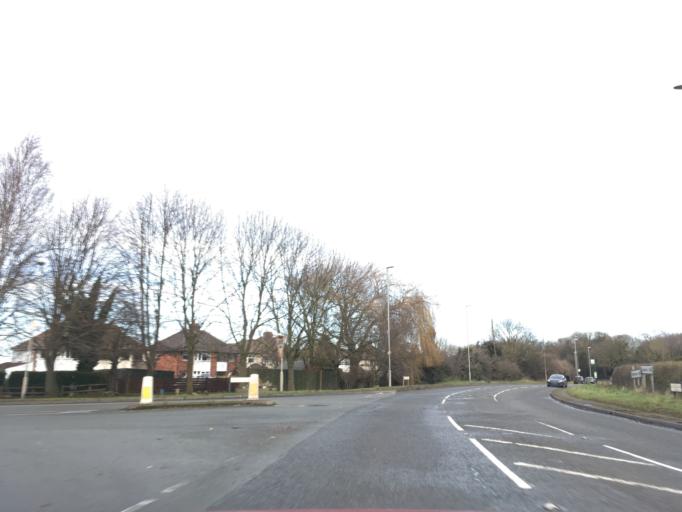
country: GB
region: England
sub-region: Nottinghamshire
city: Ruddington
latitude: 52.8558
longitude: -1.1370
